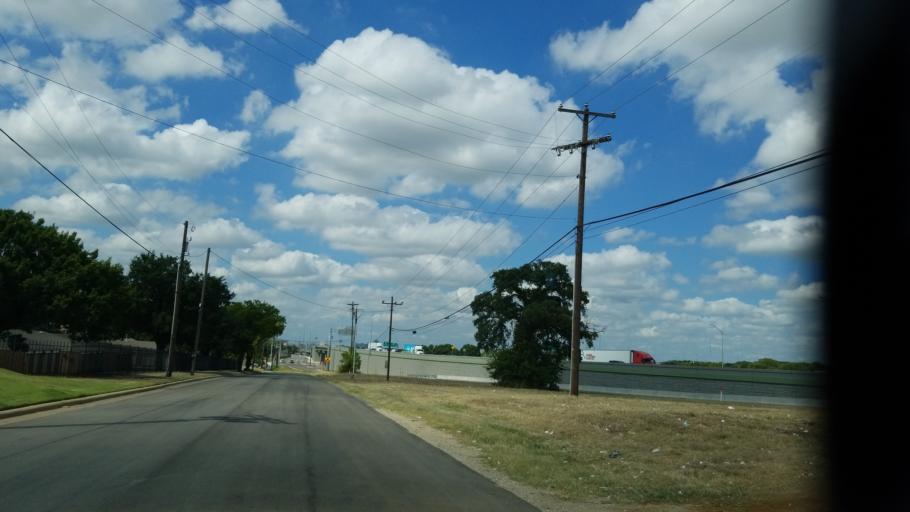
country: US
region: Texas
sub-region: Tarrant County
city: Euless
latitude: 32.8372
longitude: -97.0866
